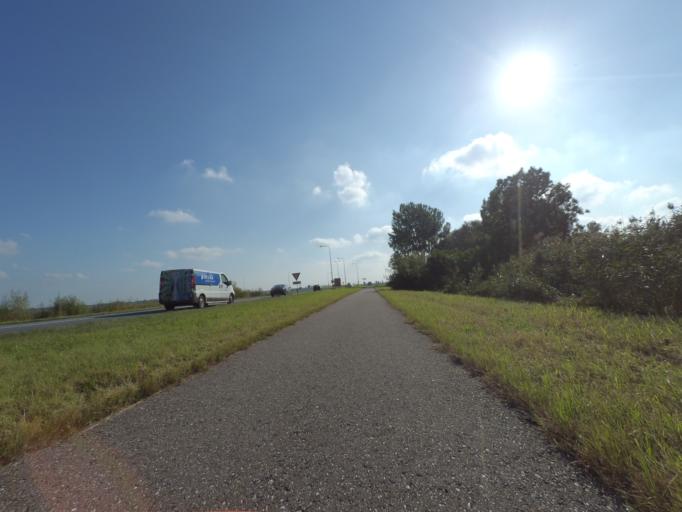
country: NL
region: Gelderland
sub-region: Gemeente Nijkerk
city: Nijkerk
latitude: 52.2582
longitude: 5.4729
